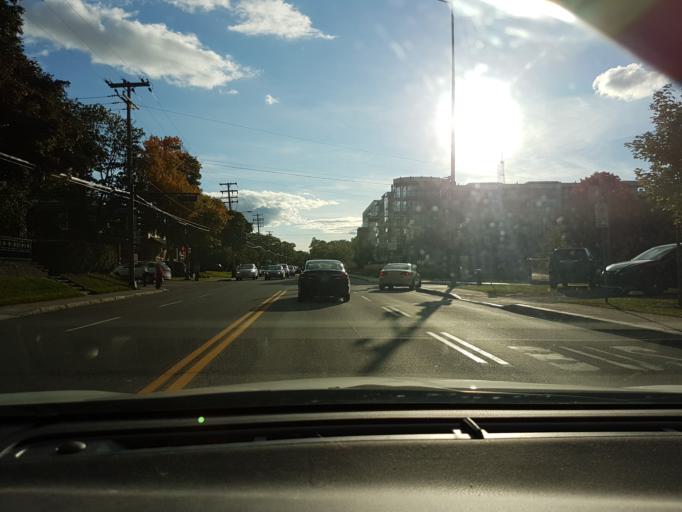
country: CA
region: Quebec
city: Quebec
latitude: 46.7866
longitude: -71.2576
